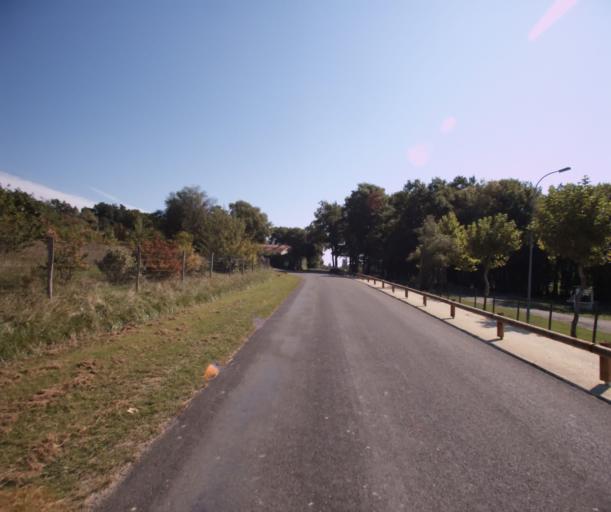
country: FR
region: Midi-Pyrenees
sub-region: Departement du Gers
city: Cazaubon
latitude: 43.9387
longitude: -0.0405
